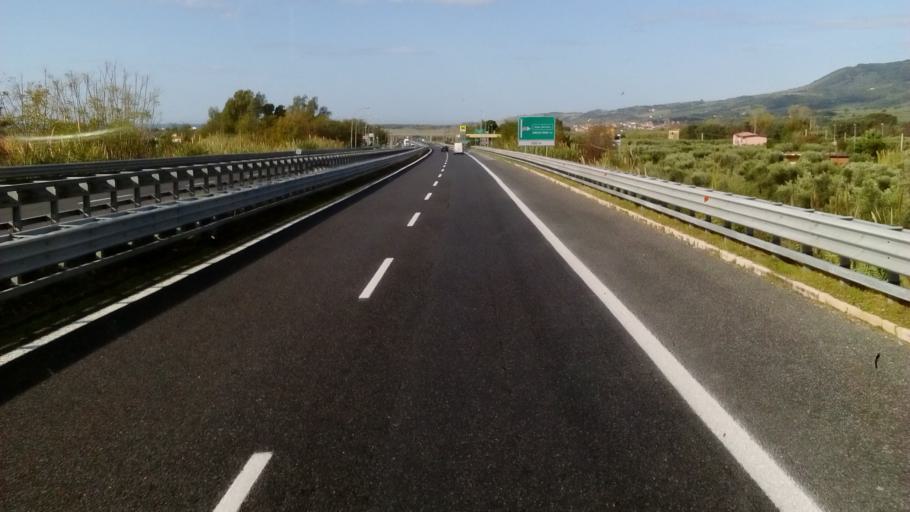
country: IT
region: Calabria
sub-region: Provincia di Catanzaro
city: Santa Eufemia Lamezia
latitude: 38.9286
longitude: 16.2418
